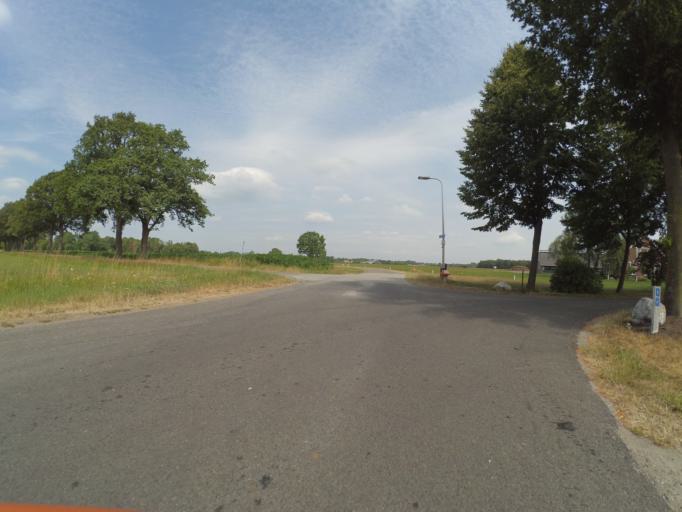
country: NL
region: Overijssel
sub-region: Gemeente Hof van Twente
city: Hengevelde
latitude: 52.1743
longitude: 6.6040
